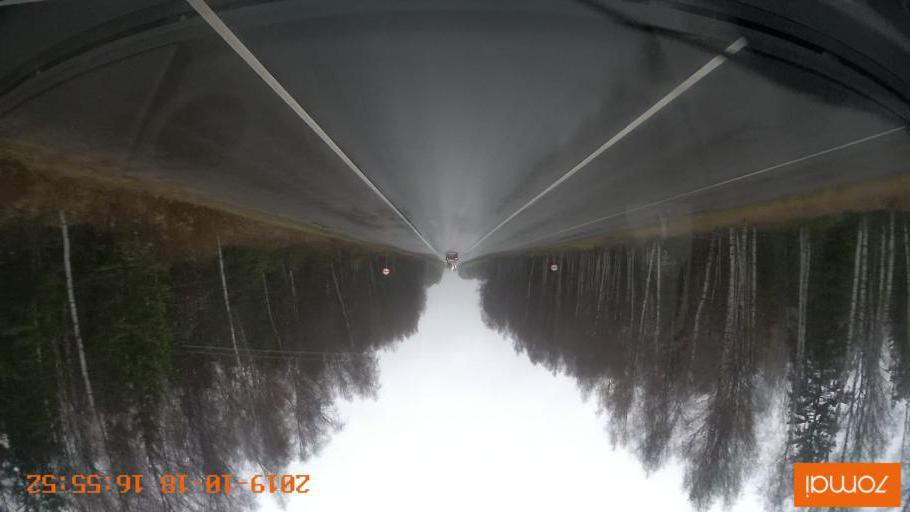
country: RU
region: Ivanovo
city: Novoye Leushino
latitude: 56.6499
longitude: 40.5834
